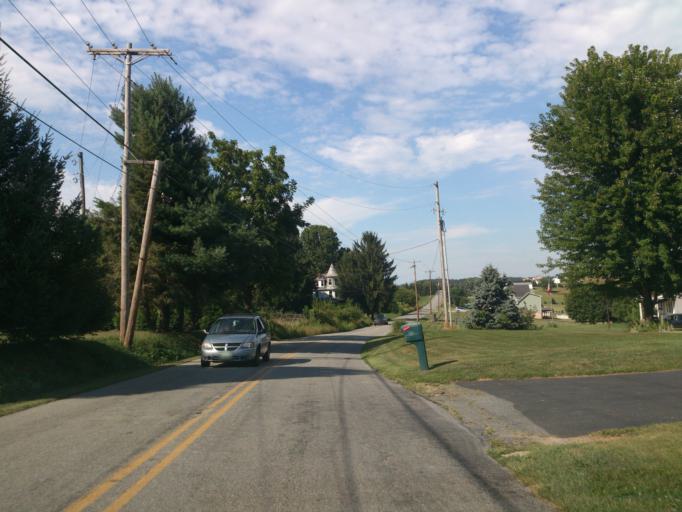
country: US
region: Pennsylvania
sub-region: York County
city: Windsor
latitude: 39.9211
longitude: -76.5278
